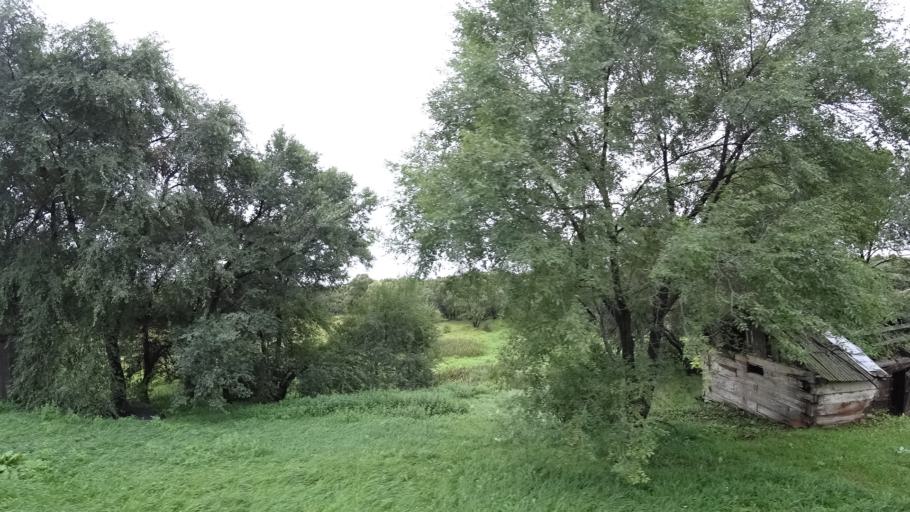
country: RU
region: Primorskiy
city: Monastyrishche
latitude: 44.2702
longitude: 132.4043
